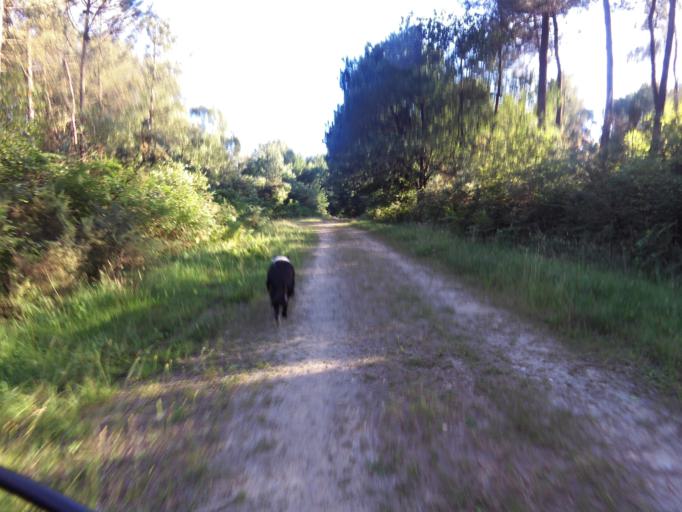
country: FR
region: Brittany
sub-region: Departement du Morbihan
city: Molac
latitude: 47.7548
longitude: -2.4114
